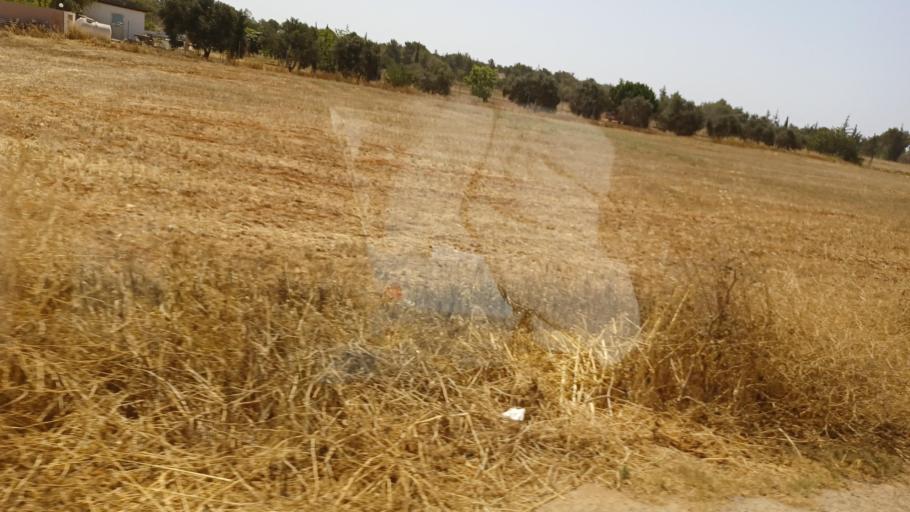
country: CY
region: Ammochostos
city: Paralimni
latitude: 35.0109
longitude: 33.9561
